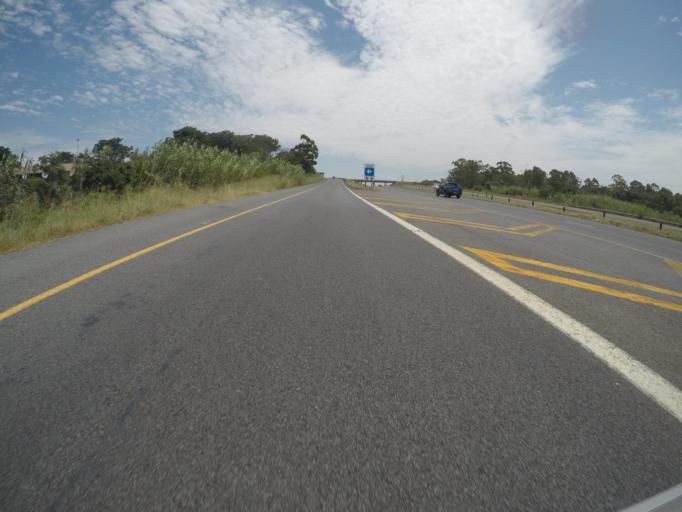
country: ZA
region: Eastern Cape
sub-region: Buffalo City Metropolitan Municipality
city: East London
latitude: -32.9712
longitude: 27.8548
